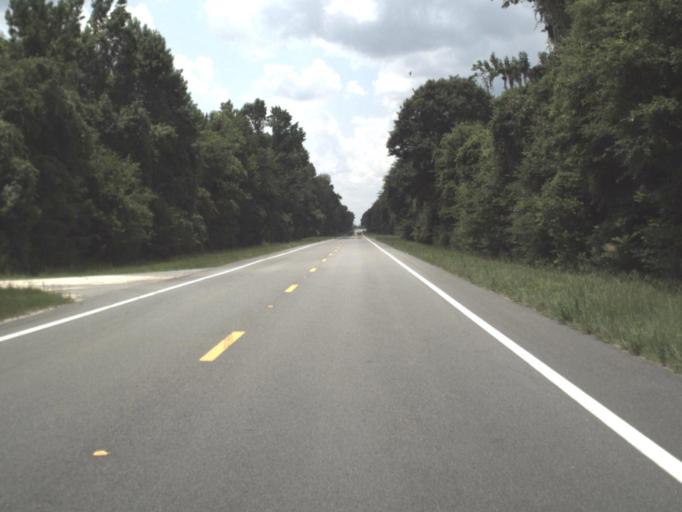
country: US
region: Florida
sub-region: Hamilton County
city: Jasper
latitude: 30.4811
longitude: -82.9185
